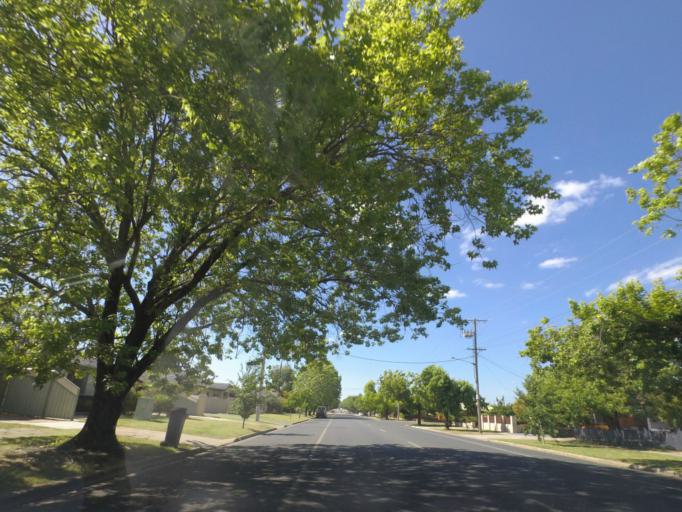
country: AU
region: New South Wales
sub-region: Albury Municipality
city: South Albury
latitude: -36.0886
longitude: 146.9141
